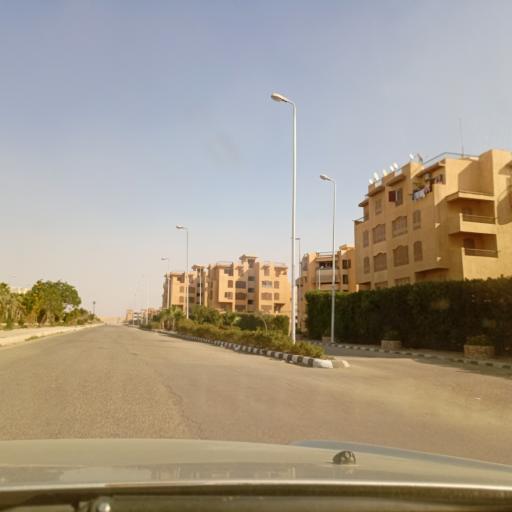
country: EG
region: Muhafazat al Qalyubiyah
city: Al Khankah
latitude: 30.0458
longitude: 31.4875
